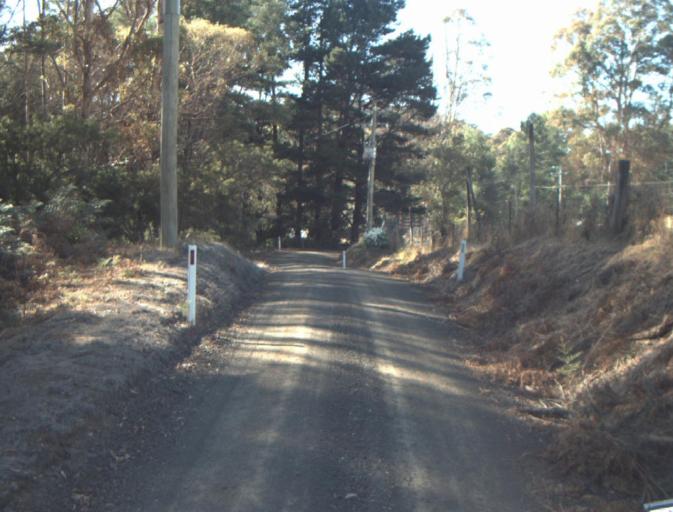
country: AU
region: Tasmania
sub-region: Launceston
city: Mayfield
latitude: -41.2946
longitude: 147.1981
